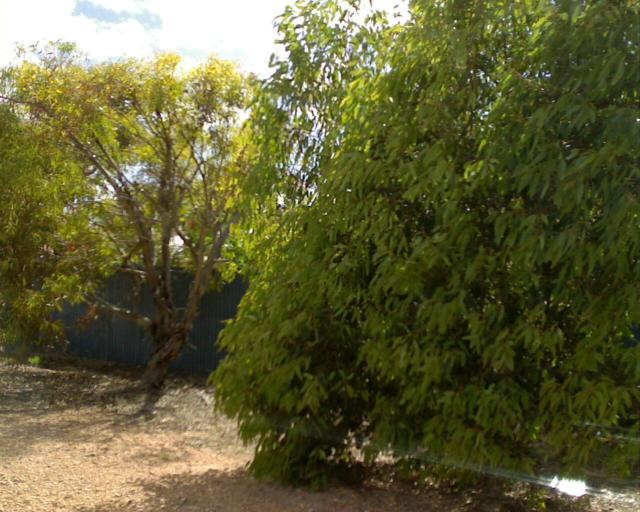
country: AU
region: South Australia
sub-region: Ceduna
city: Ceduna
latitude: -32.1020
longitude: 133.5768
